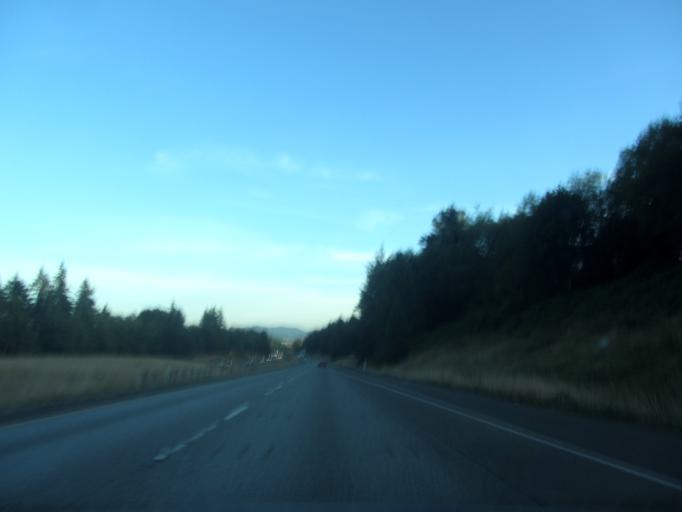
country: US
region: Washington
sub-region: Skagit County
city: Burlington
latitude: 48.5314
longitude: -122.3525
